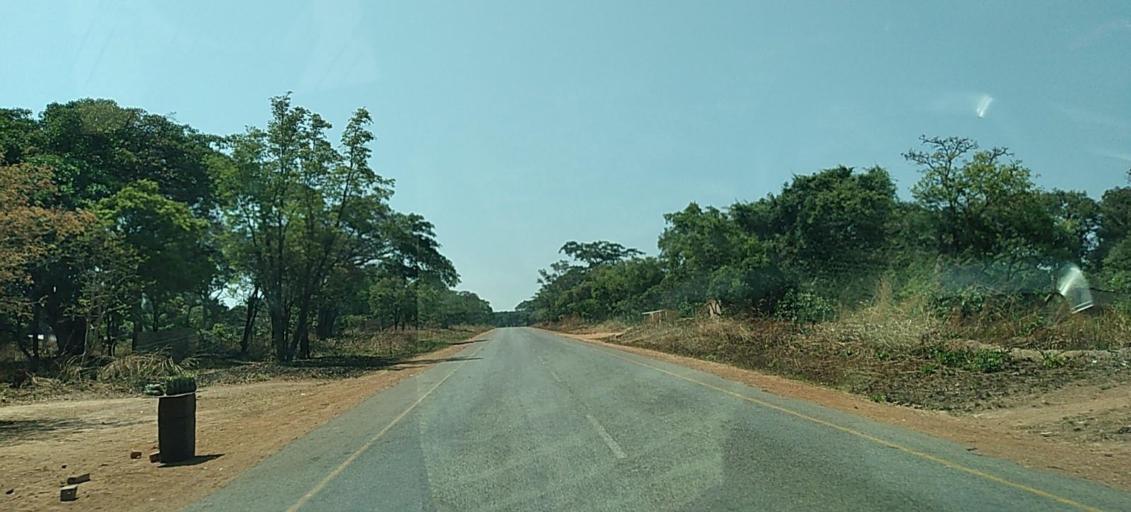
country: ZM
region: North-Western
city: Solwezi
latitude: -12.2940
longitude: 25.6998
